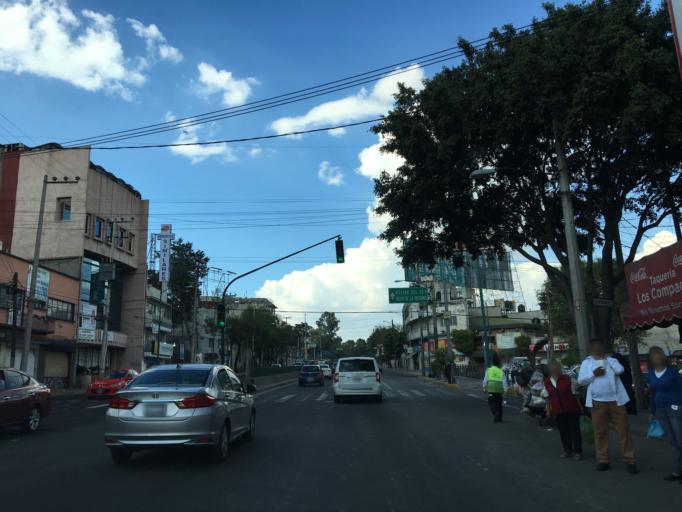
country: MX
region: Mexico City
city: Polanco
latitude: 19.4102
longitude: -99.1907
